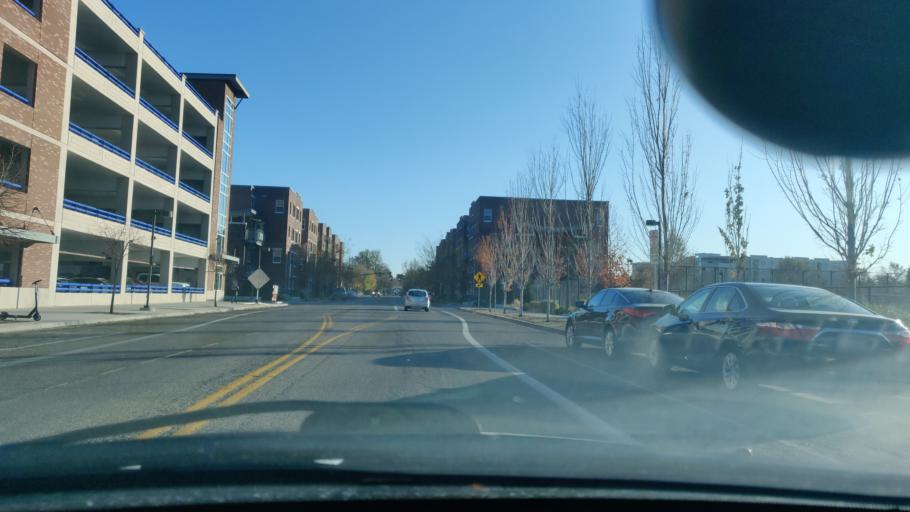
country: US
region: Idaho
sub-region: Ada County
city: Boise
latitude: 43.6004
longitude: -116.2024
